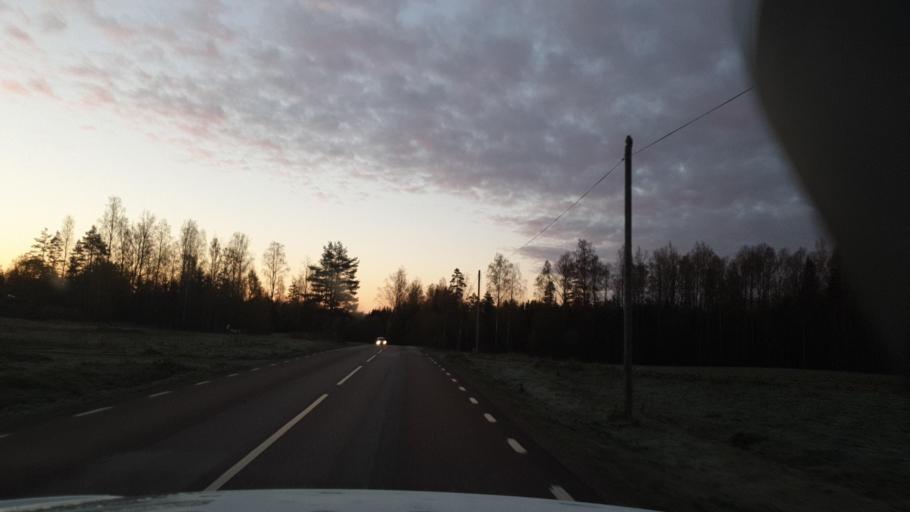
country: SE
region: Vaermland
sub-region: Eda Kommun
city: Amotfors
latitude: 59.7781
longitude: 12.2674
